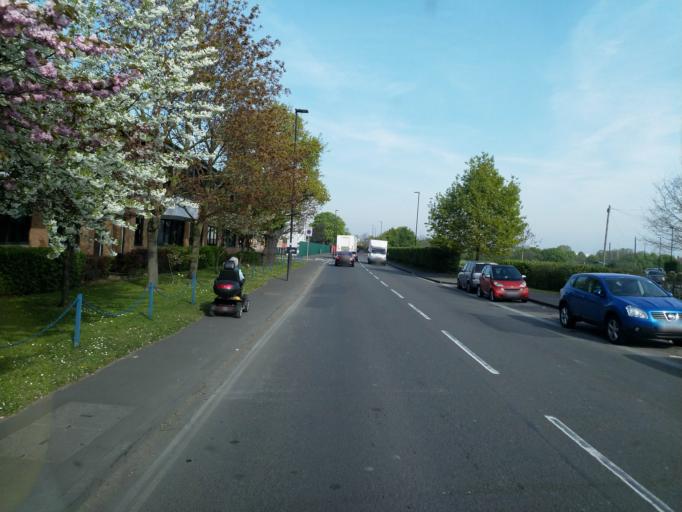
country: GB
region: England
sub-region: Greater London
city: Feltham
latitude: 51.4694
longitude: -0.4042
